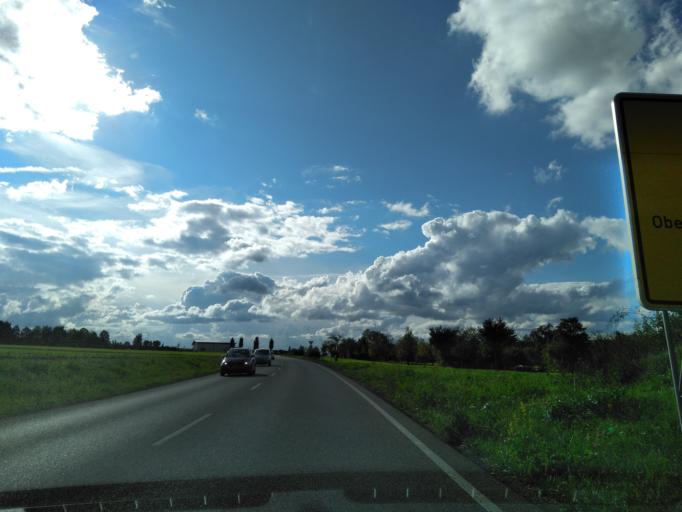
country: DE
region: Baden-Wuerttemberg
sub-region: Regierungsbezirk Stuttgart
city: Sersheim
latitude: 48.9504
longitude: 9.0213
